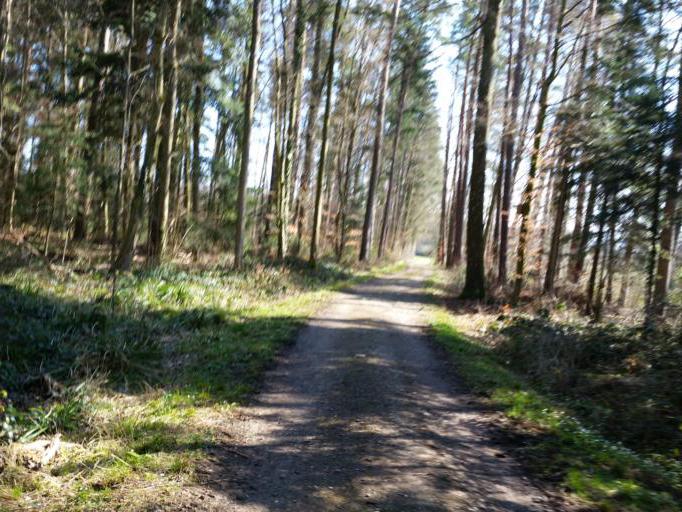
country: CH
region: Saint Gallen
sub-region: Wahlkreis St. Gallen
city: Muolen
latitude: 47.5438
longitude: 9.3221
